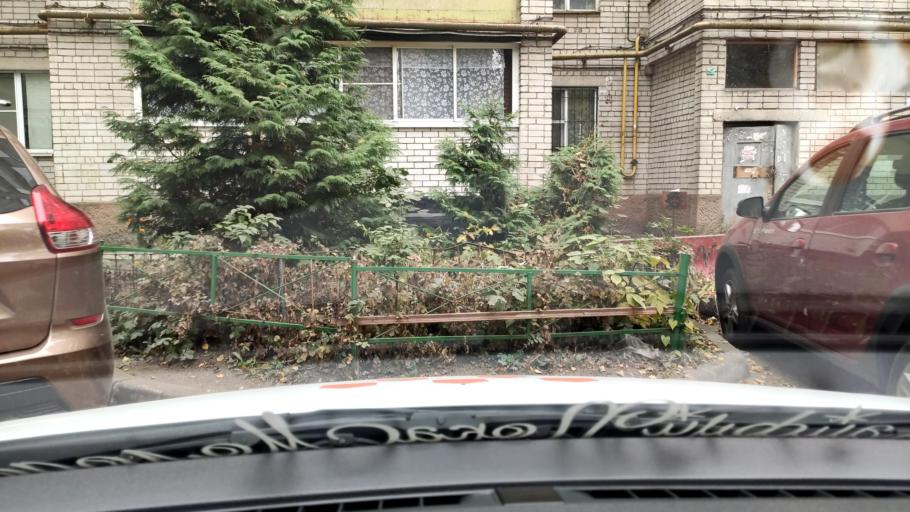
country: RU
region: Voronezj
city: Podgornoye
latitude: 51.7085
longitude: 39.1660
